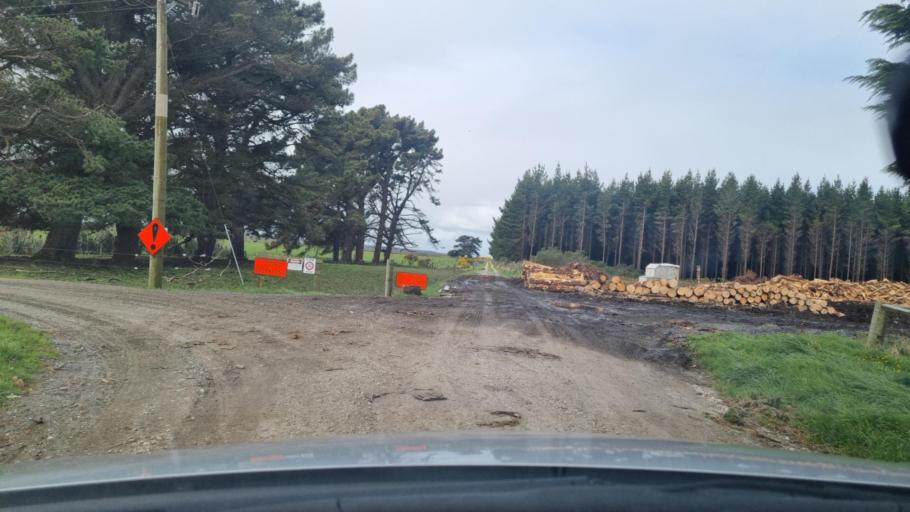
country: NZ
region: Southland
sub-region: Invercargill City
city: Invercargill
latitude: -46.4920
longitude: 168.4383
